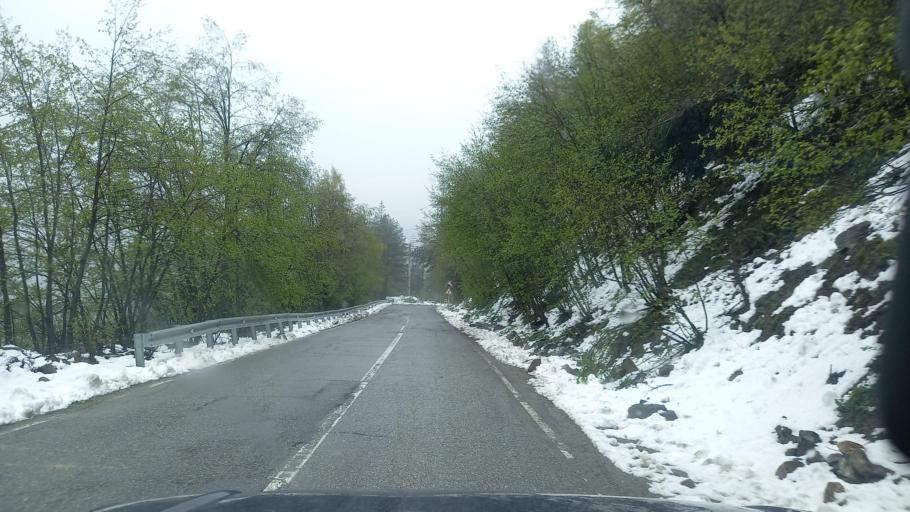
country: RU
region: North Ossetia
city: Mizur
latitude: 42.8006
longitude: 43.9312
